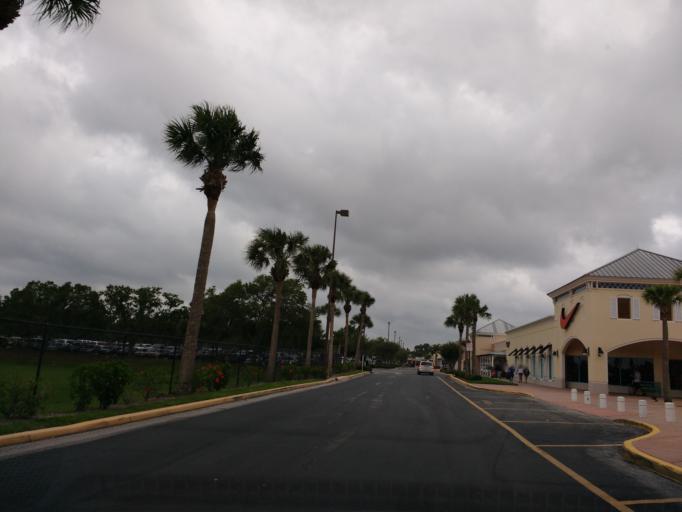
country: US
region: Florida
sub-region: Manatee County
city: Ellenton
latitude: 27.5363
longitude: -82.5067
